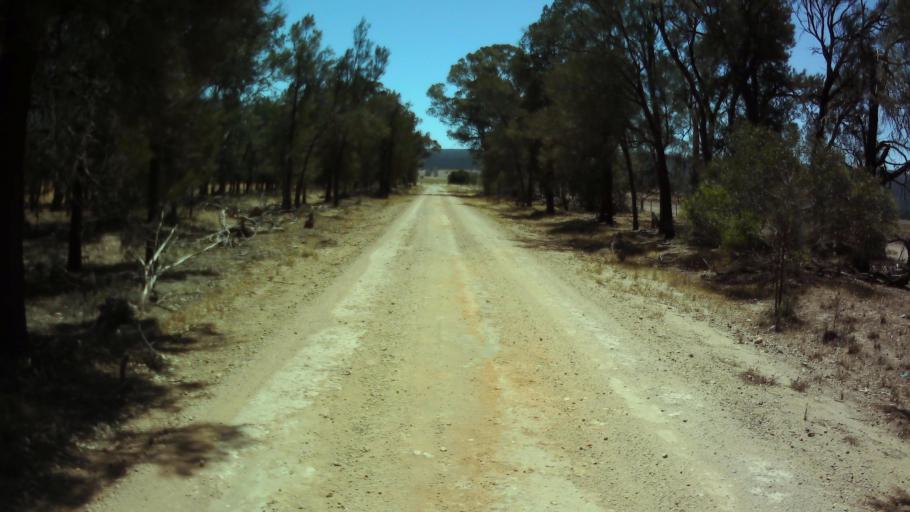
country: AU
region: New South Wales
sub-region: Weddin
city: Grenfell
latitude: -33.9952
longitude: 147.9579
